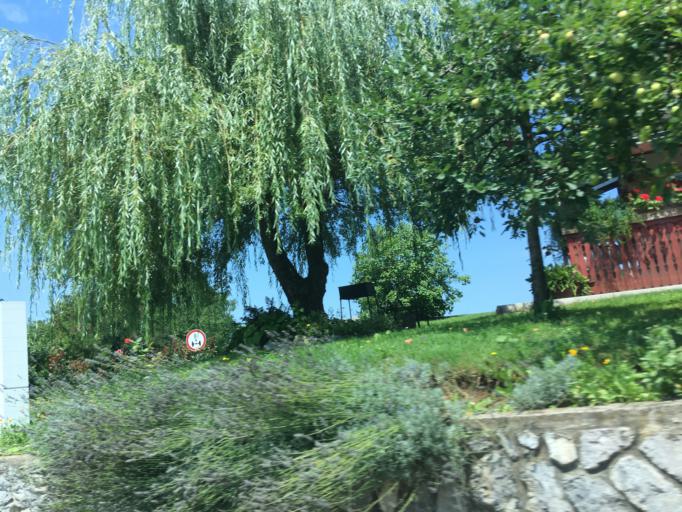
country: SI
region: Metlika
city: Metlika
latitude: 45.6485
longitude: 15.3370
